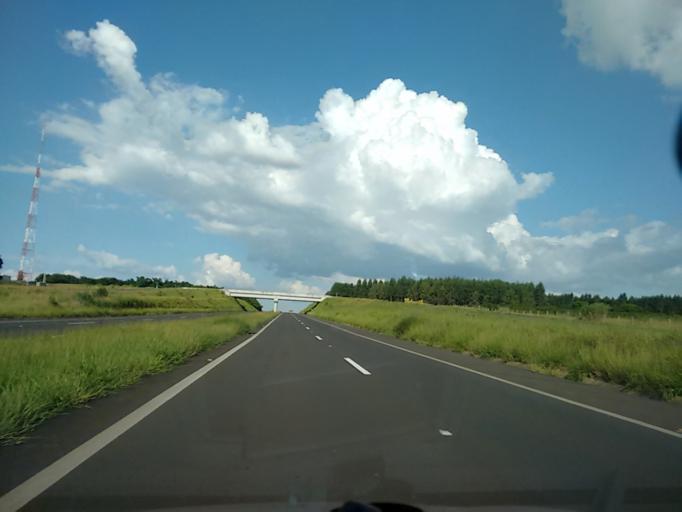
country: BR
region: Sao Paulo
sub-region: Duartina
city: Duartina
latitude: -22.3302
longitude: -49.4537
